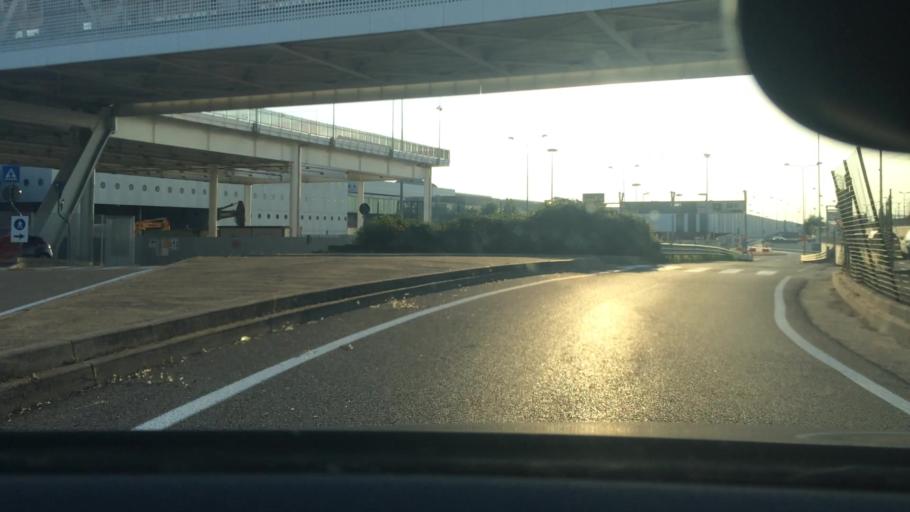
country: IT
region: Lombardy
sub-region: Citta metropolitana di Milano
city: Pero
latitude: 45.5211
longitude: 9.0877
